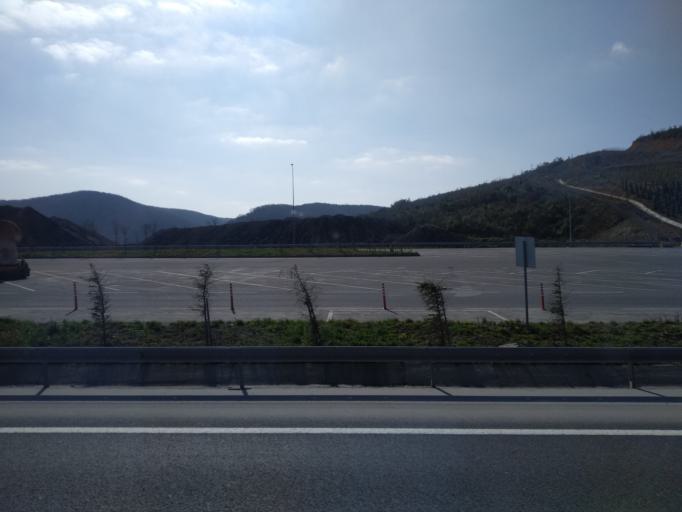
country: TR
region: Istanbul
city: Arikoey
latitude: 41.2243
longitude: 28.9870
